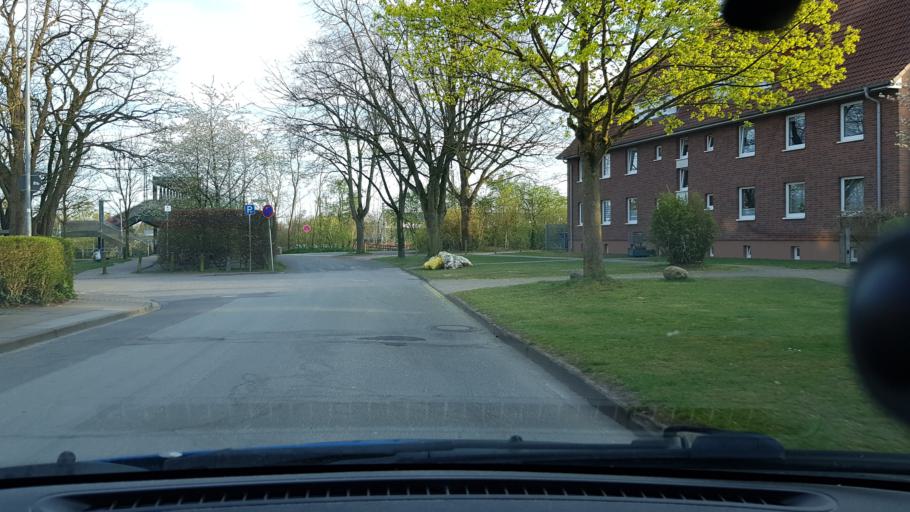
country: DE
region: Lower Saxony
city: Buchholz in der Nordheide
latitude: 53.3256
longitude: 9.8732
